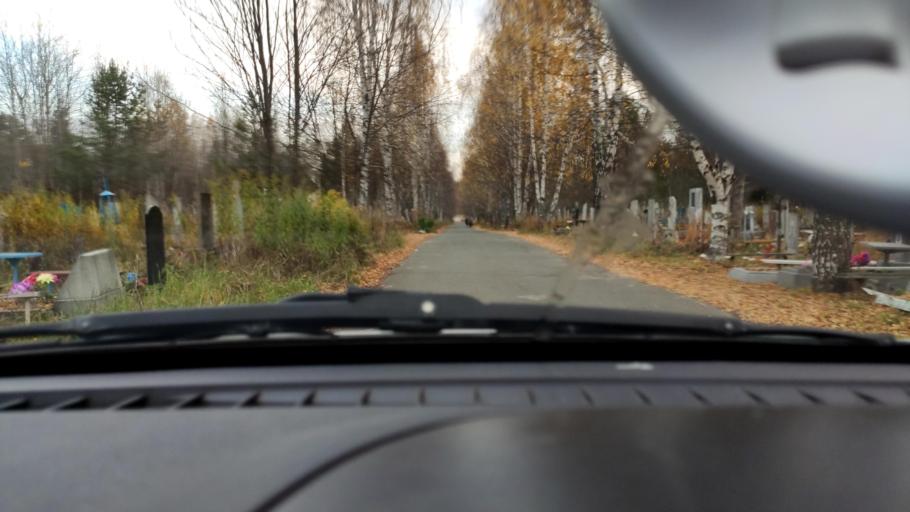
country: RU
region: Perm
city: Kondratovo
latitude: 58.0652
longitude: 56.1346
